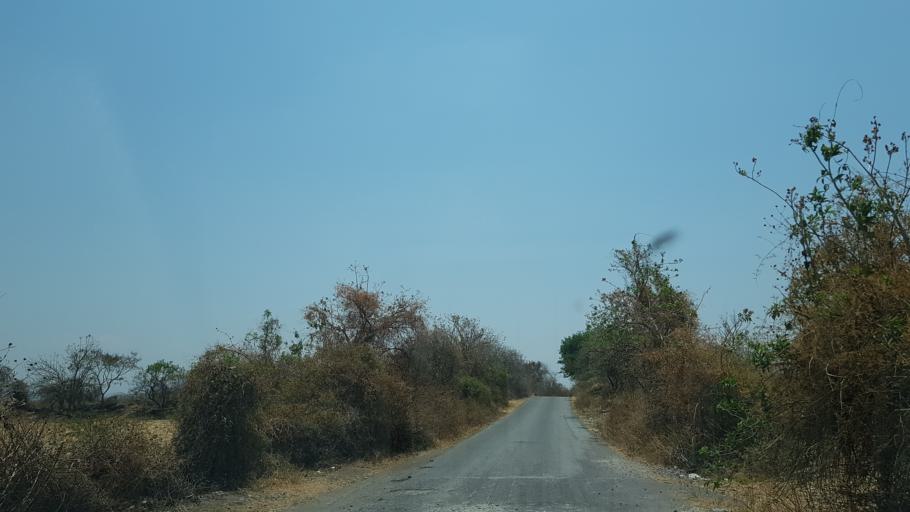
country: MX
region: Puebla
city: Huaquechula
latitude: 18.7867
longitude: -98.5448
